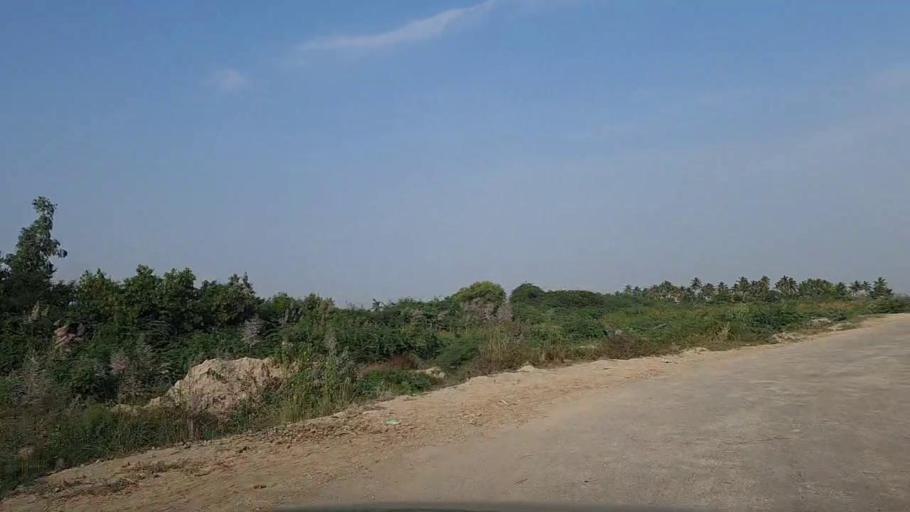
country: PK
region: Sindh
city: Thatta
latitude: 24.6511
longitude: 67.9123
